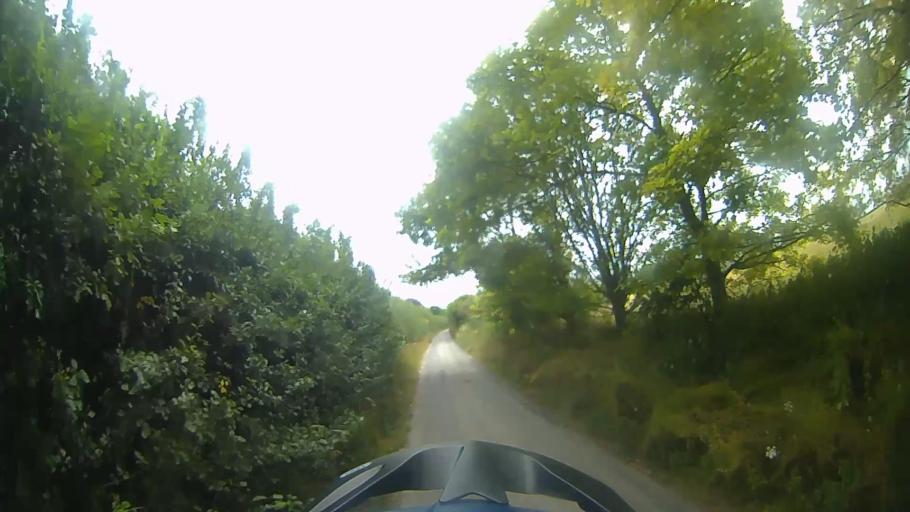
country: GB
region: England
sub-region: Oxfordshire
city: Wantage
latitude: 51.5707
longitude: -1.4490
